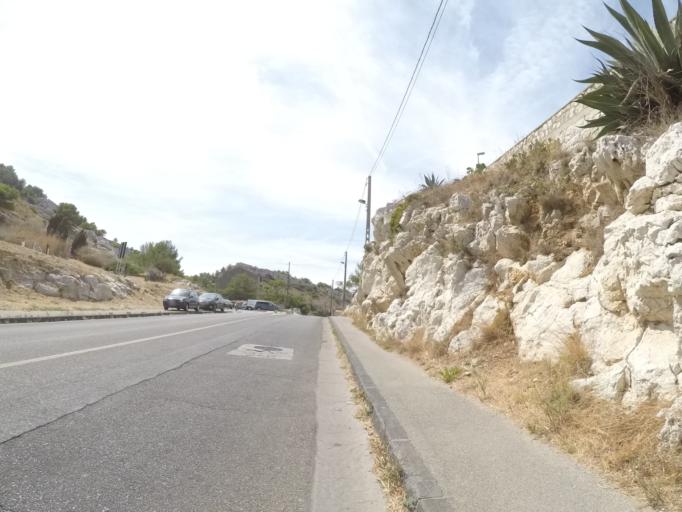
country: FR
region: Provence-Alpes-Cote d'Azur
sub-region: Departement des Bouches-du-Rhone
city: Marseille 08
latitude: 43.2298
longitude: 5.3543
